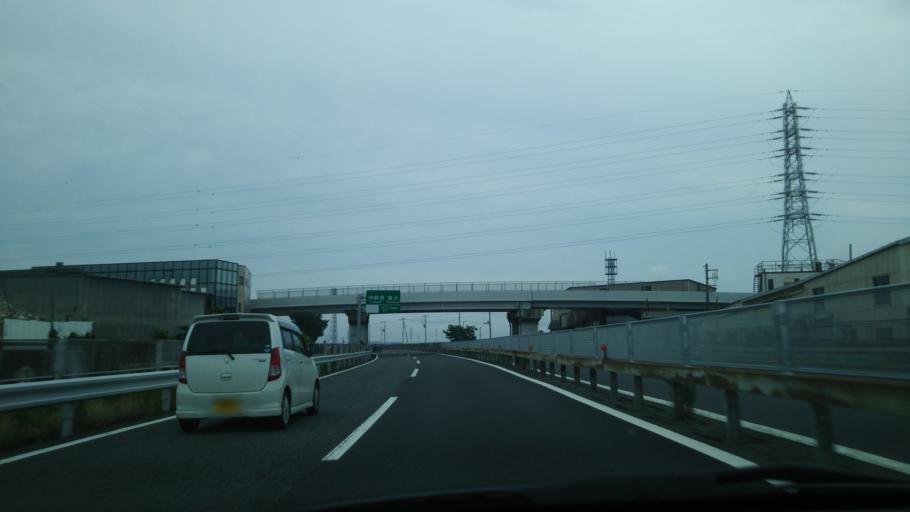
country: JP
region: Kanagawa
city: Isehara
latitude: 35.3762
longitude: 139.3254
